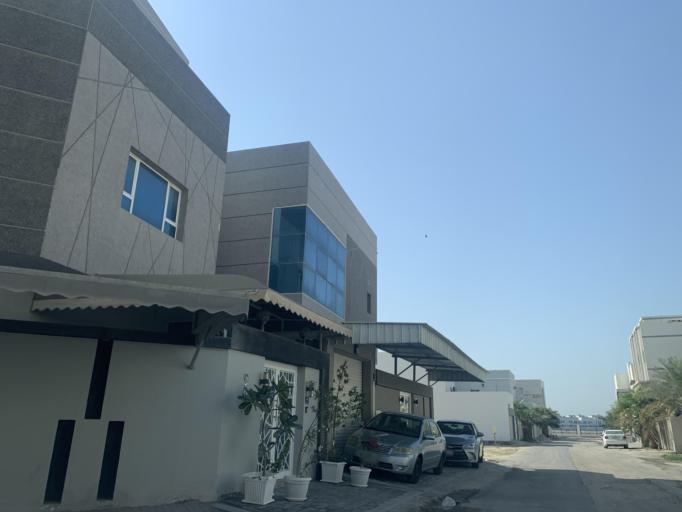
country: BH
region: Central Governorate
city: Madinat Hamad
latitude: 26.1323
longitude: 50.4877
